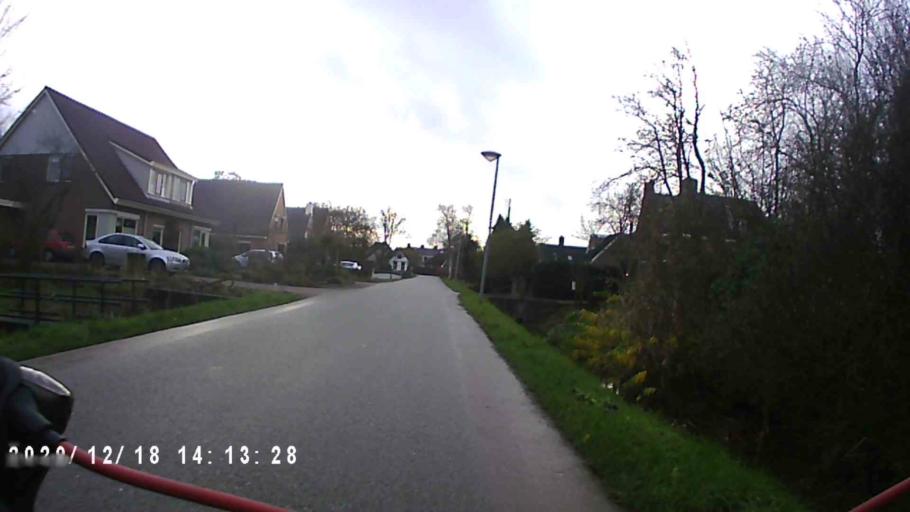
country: NL
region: Groningen
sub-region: Gemeente Bedum
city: Bedum
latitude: 53.2707
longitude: 6.6533
